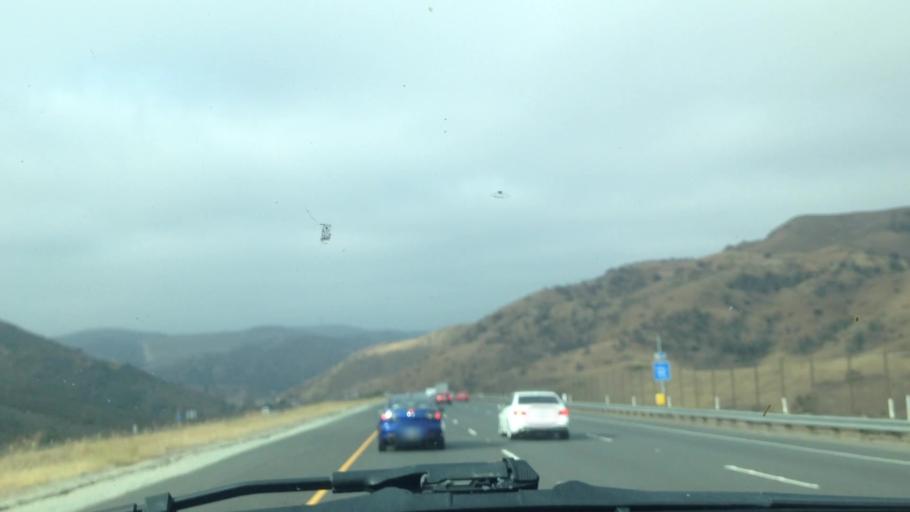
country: US
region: California
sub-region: Orange County
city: North Tustin
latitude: 33.8122
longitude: -117.7210
